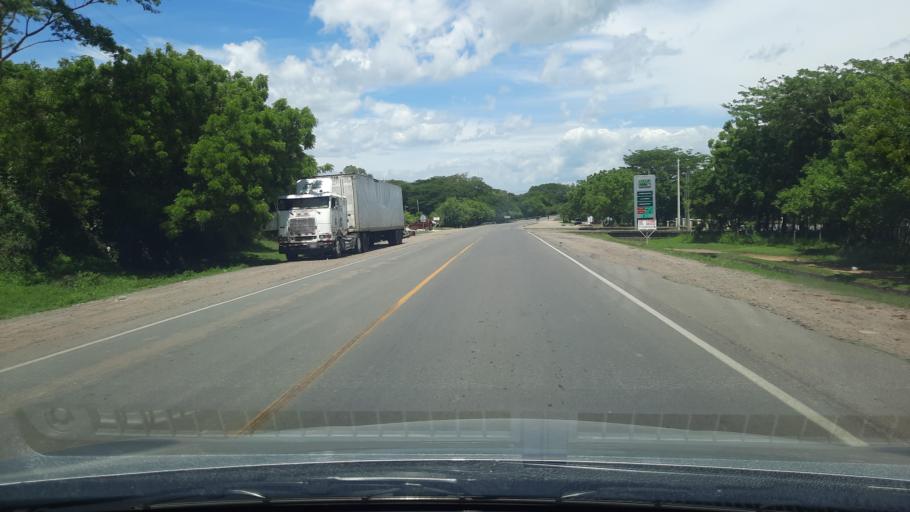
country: NI
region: Chinandega
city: Somotillo
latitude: 13.0512
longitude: -86.9078
